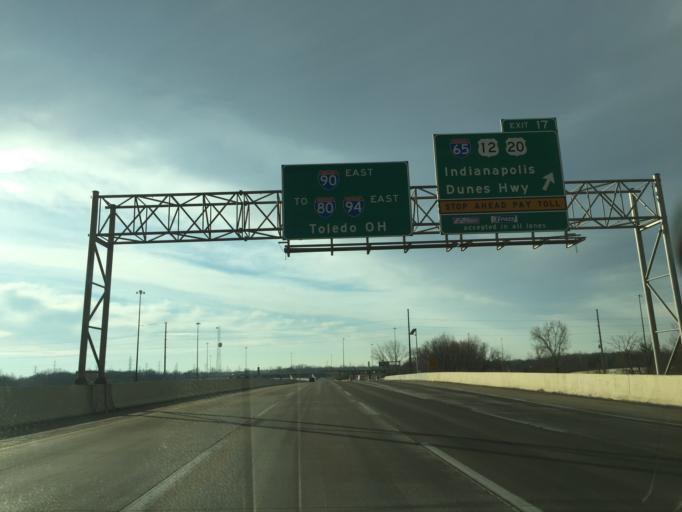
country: US
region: Indiana
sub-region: Lake County
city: Gary
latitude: 41.5960
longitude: -87.3055
